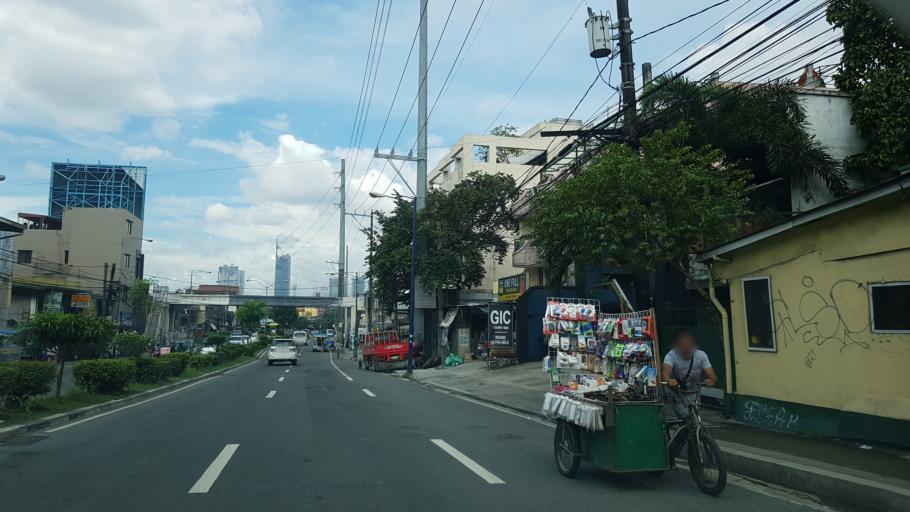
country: PH
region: Metro Manila
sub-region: Makati City
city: Makati City
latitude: 14.5601
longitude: 121.0478
